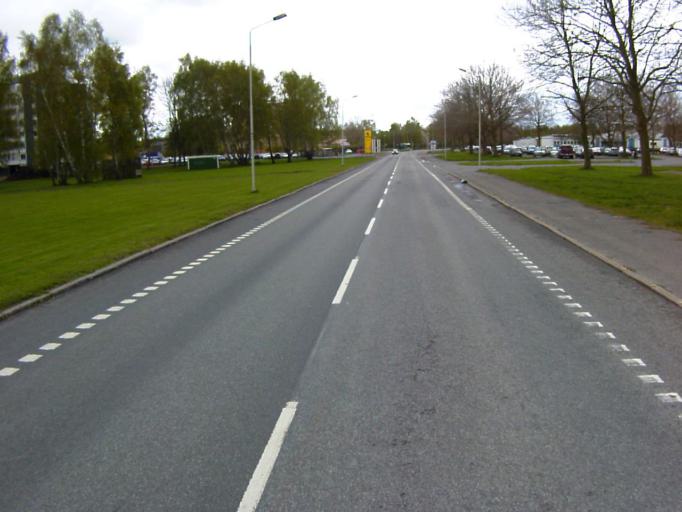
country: SE
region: Skane
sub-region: Kristianstads Kommun
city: Kristianstad
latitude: 56.0446
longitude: 14.1766
